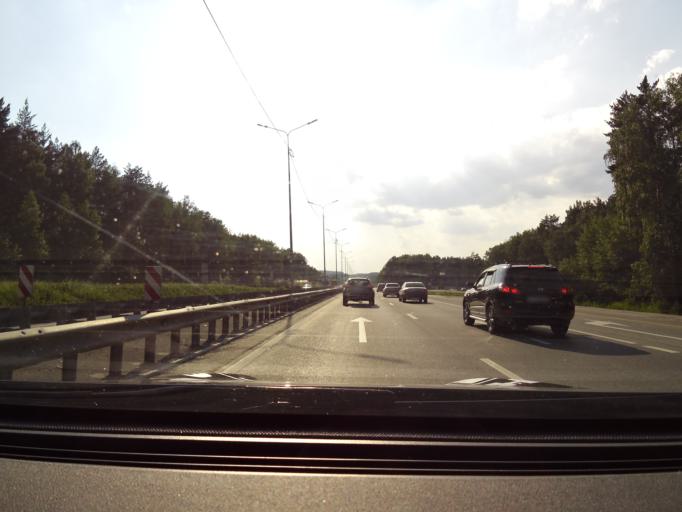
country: RU
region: Sverdlovsk
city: Shirokaya Rechka
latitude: 56.8270
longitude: 60.4364
